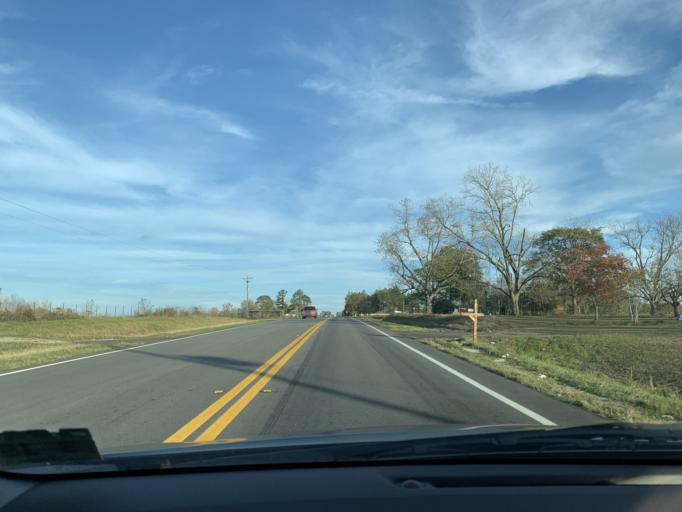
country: US
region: Georgia
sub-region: Irwin County
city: Ocilla
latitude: 31.5959
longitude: -83.1599
